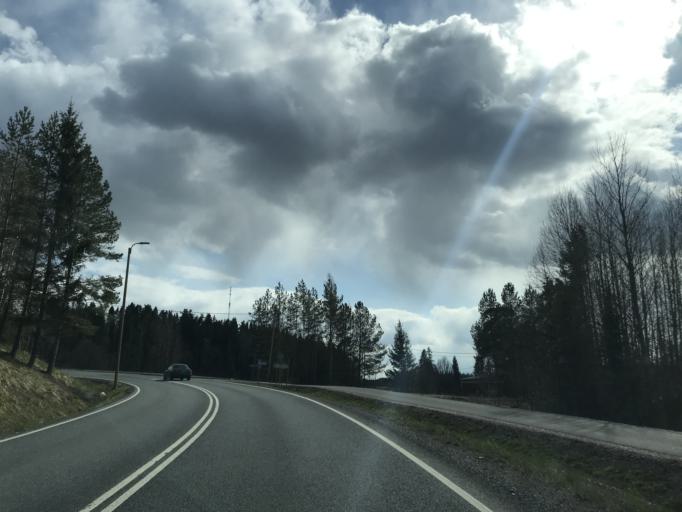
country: FI
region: Uusimaa
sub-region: Helsinki
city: Jaervenpaeae
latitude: 60.4831
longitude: 25.0420
